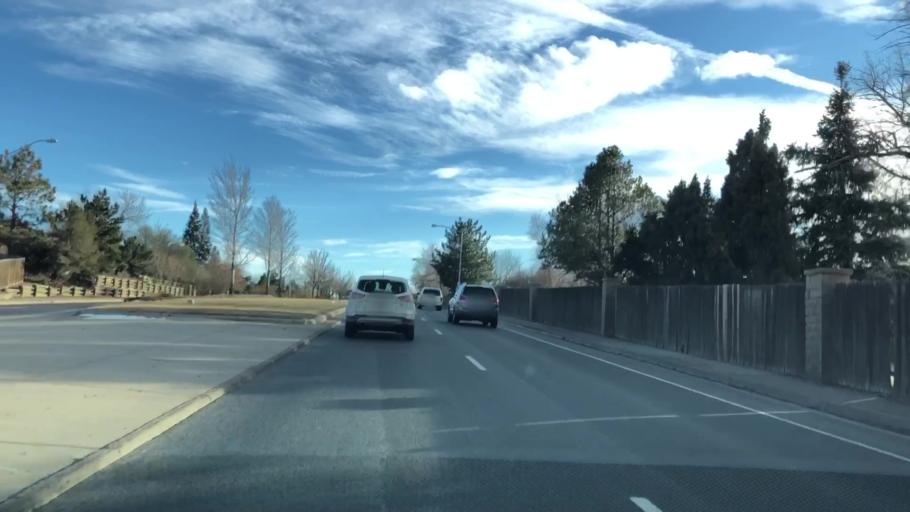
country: US
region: Colorado
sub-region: Arapahoe County
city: Dove Valley
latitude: 39.6440
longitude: -104.7917
